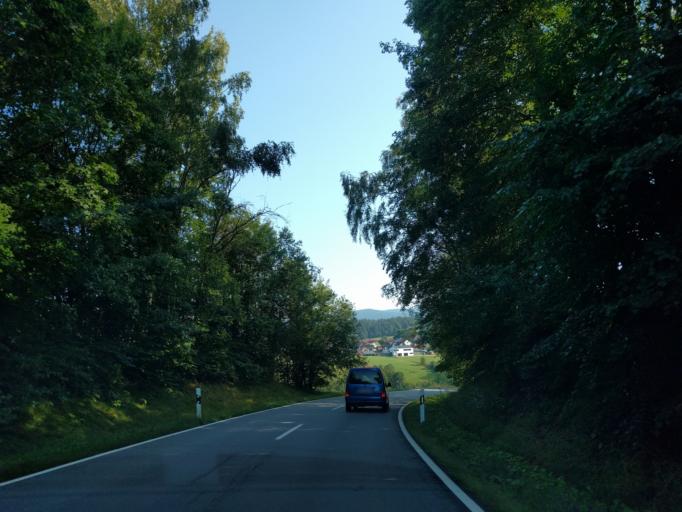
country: DE
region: Bavaria
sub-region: Lower Bavaria
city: Neuschonau
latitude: 48.8637
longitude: 13.4573
